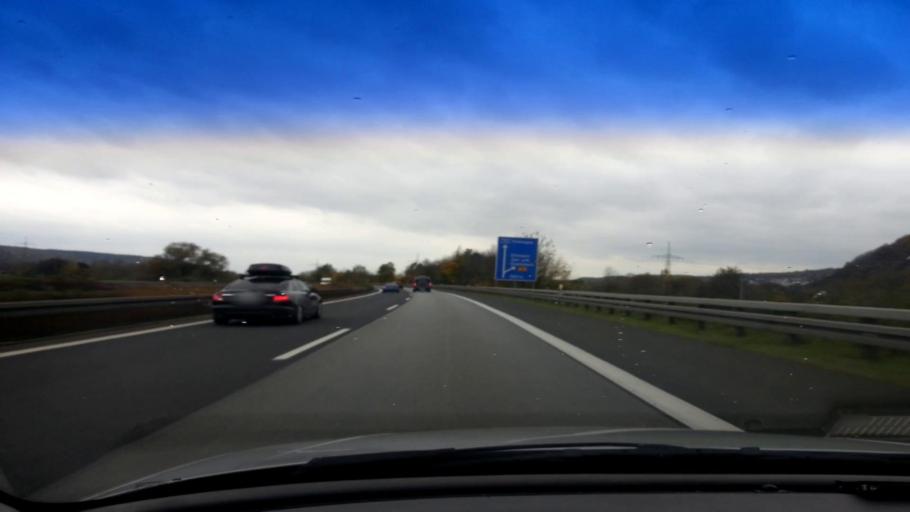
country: DE
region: Bavaria
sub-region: Regierungsbezirk Unterfranken
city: Ebelsbach
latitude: 49.9770
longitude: 10.6867
